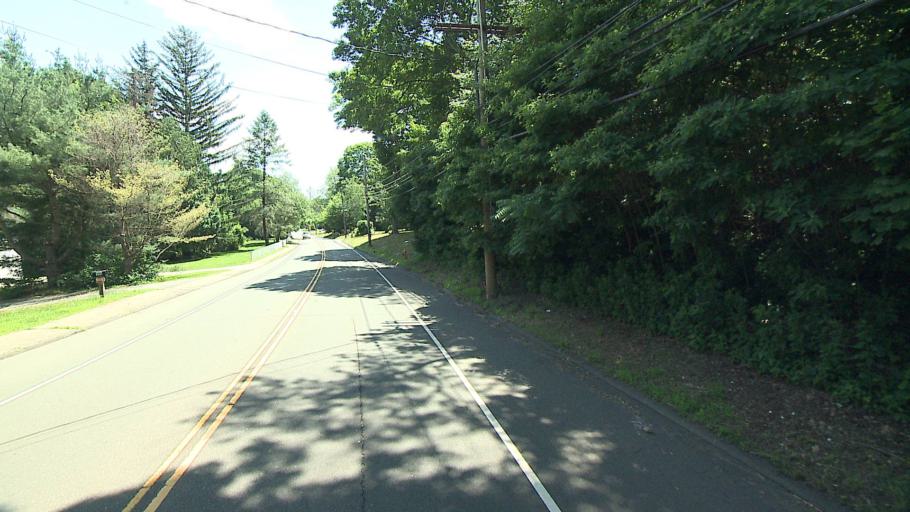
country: US
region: Connecticut
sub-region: Fairfield County
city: Trumbull
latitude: 41.2505
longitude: -73.1974
